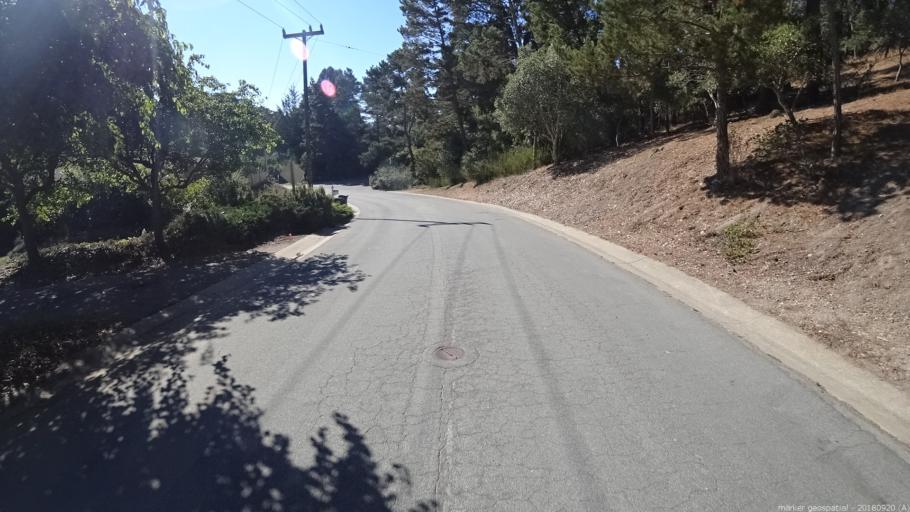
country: US
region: California
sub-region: Monterey County
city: Carmel-by-the-Sea
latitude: 36.5556
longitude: -121.8979
